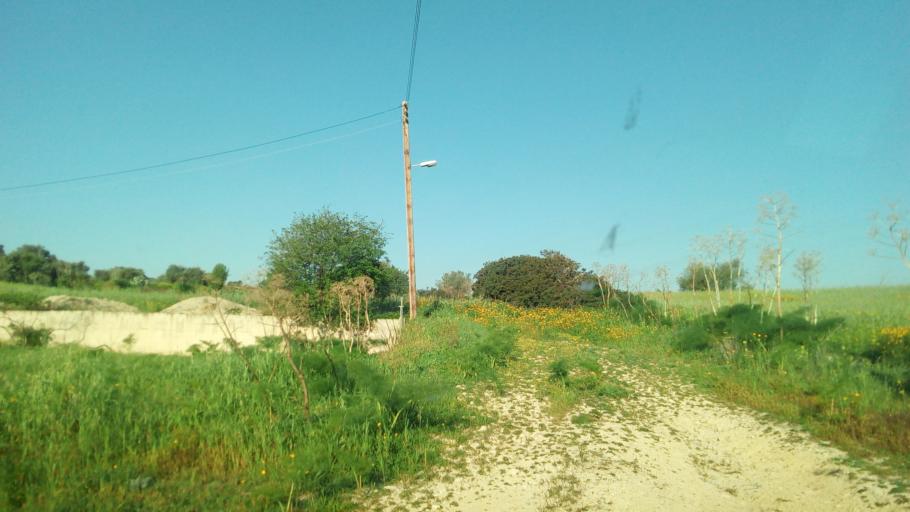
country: CY
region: Larnaka
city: Kofinou
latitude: 34.8046
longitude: 33.4319
